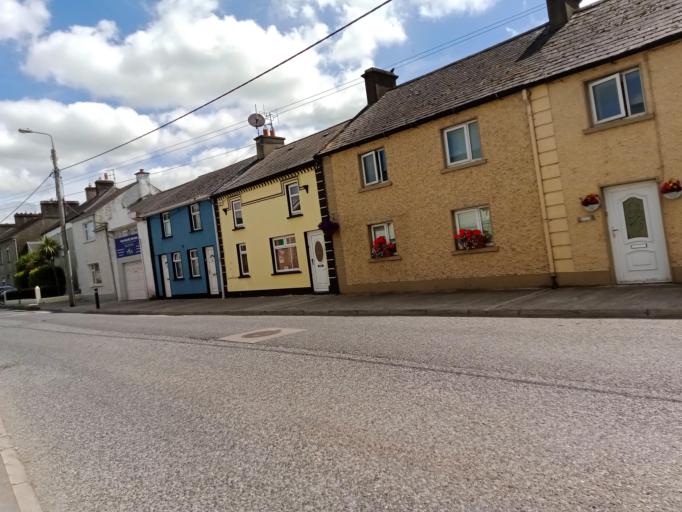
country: IE
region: Leinster
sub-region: Kilkenny
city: Callan
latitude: 52.5451
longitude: -7.3929
